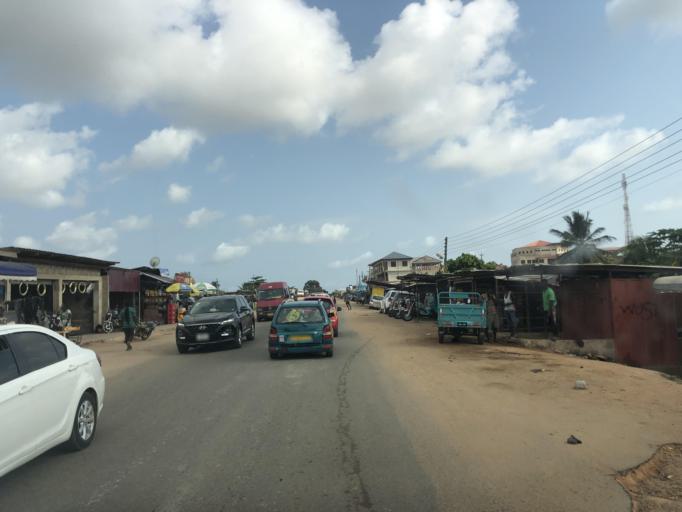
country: GH
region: Central
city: Cape Coast
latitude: 5.1435
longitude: -1.2850
